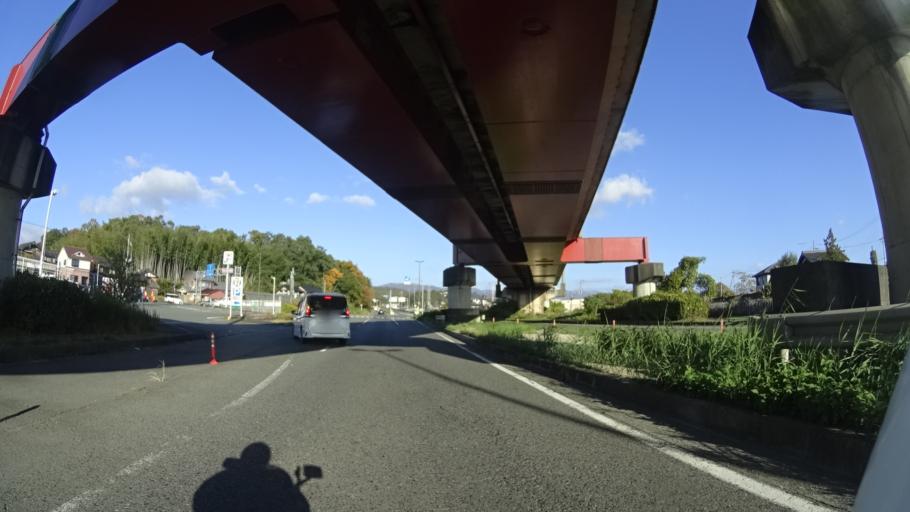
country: JP
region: Shiga Prefecture
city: Nagahama
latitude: 35.3801
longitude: 136.0337
